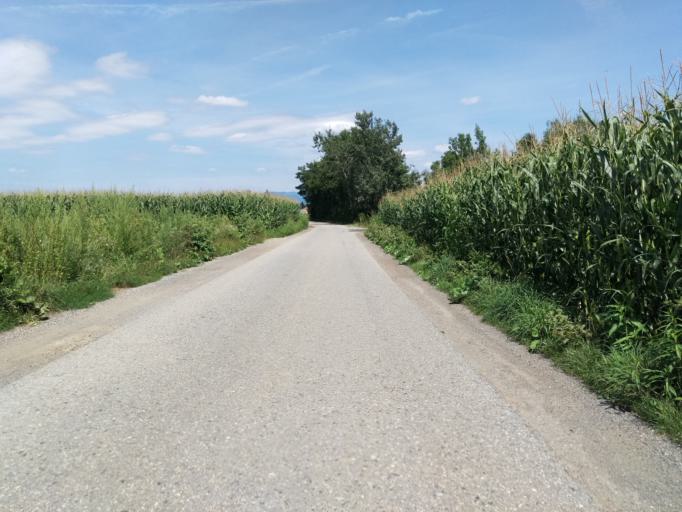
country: AT
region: Styria
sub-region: Politischer Bezirk Graz-Umgebung
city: Kalsdorf bei Graz
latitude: 46.9746
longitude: 15.4482
